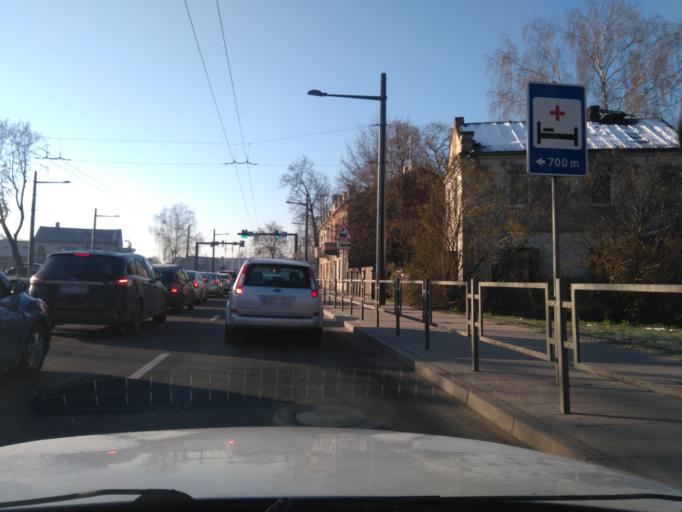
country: LT
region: Kauno apskritis
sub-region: Kaunas
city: Aleksotas
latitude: 54.8761
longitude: 23.9354
